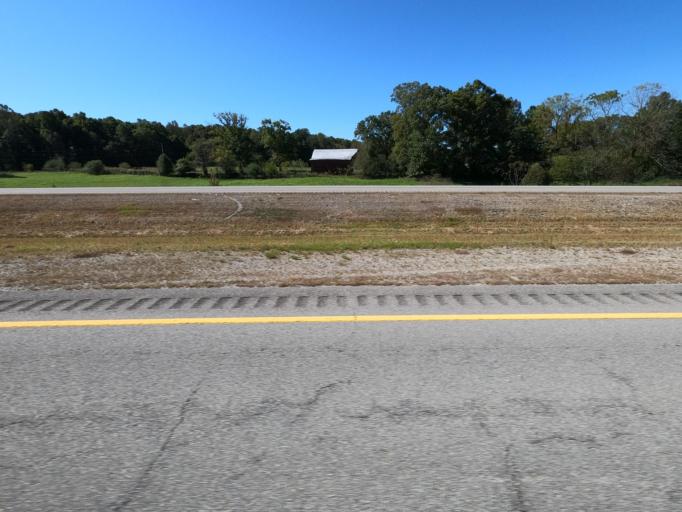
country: US
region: Tennessee
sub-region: Williamson County
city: Fairview
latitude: 35.9154
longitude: -87.1666
